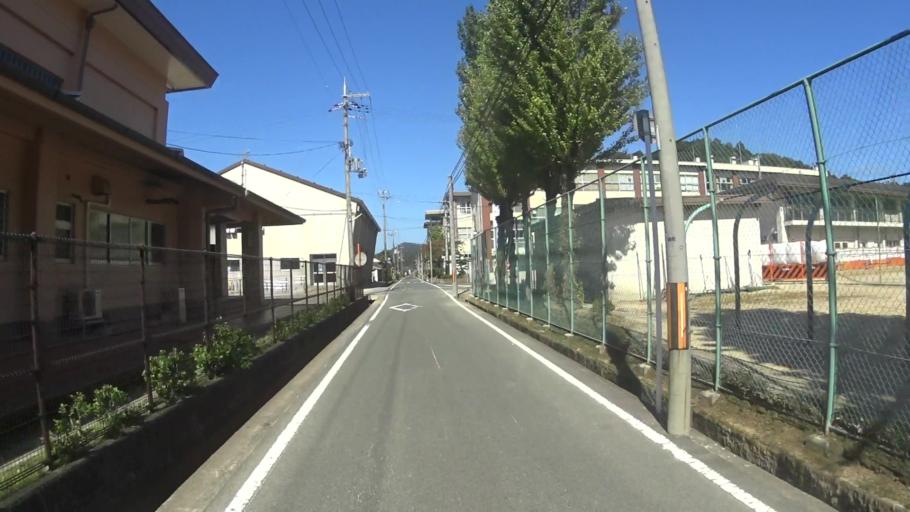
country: JP
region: Hyogo
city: Toyooka
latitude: 35.5914
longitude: 134.9317
